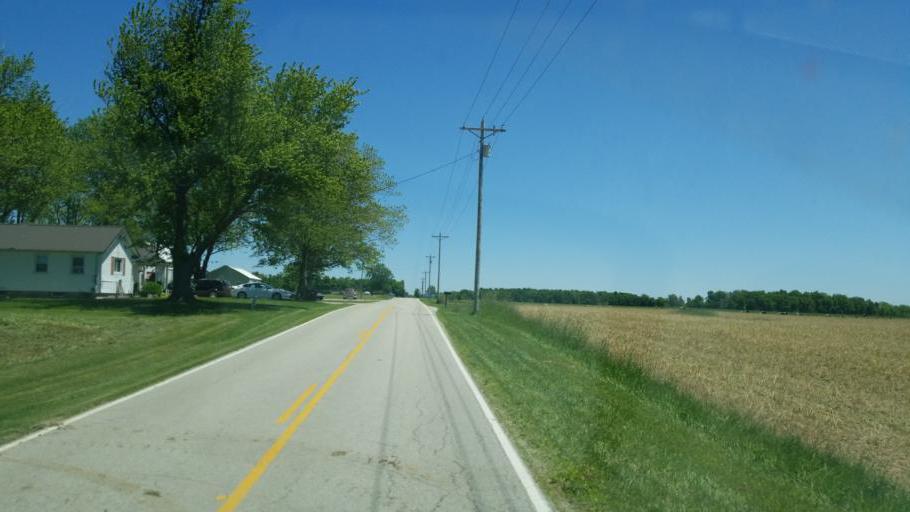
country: US
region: Ohio
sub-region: Darke County
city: Ansonia
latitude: 40.2648
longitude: -84.6613
